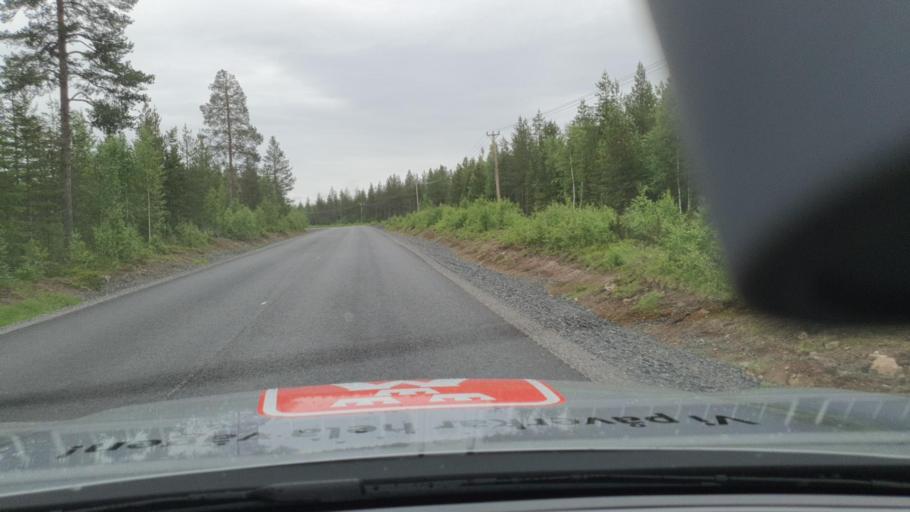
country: SE
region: Norrbotten
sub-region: Overkalix Kommun
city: OEverkalix
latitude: 66.7169
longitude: 23.1917
